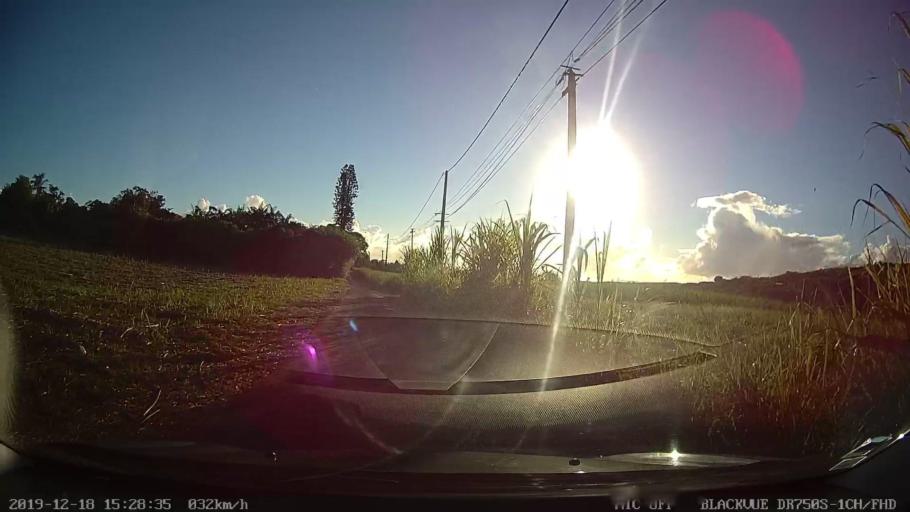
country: RE
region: Reunion
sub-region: Reunion
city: Bras-Panon
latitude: -20.9988
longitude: 55.6574
